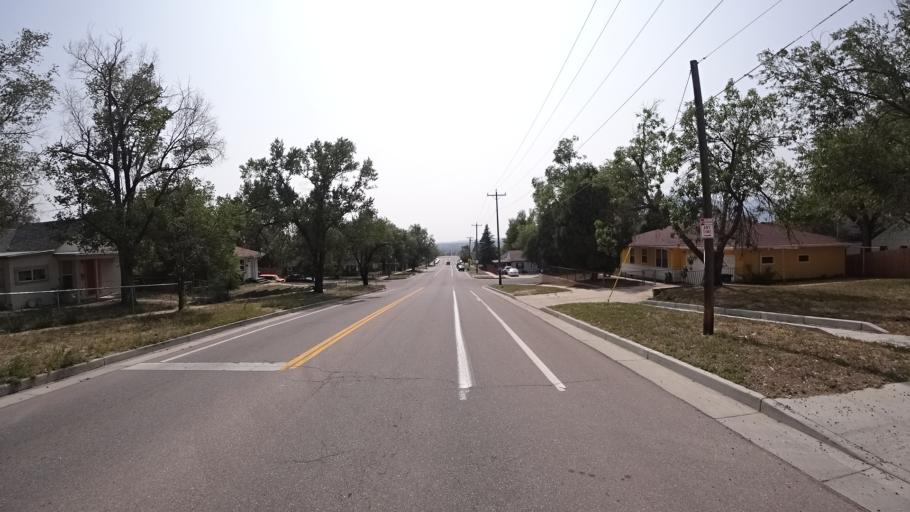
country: US
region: Colorado
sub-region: El Paso County
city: Colorado Springs
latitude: 38.8244
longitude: -104.8043
